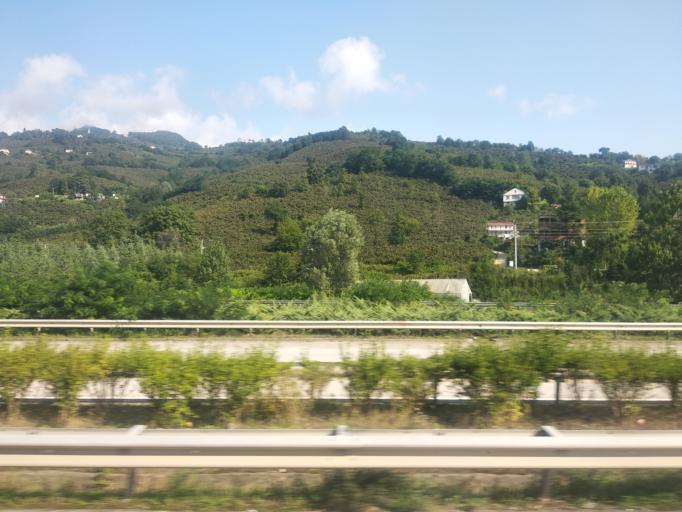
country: TR
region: Ordu
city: Ordu
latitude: 41.0057
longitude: 37.8278
